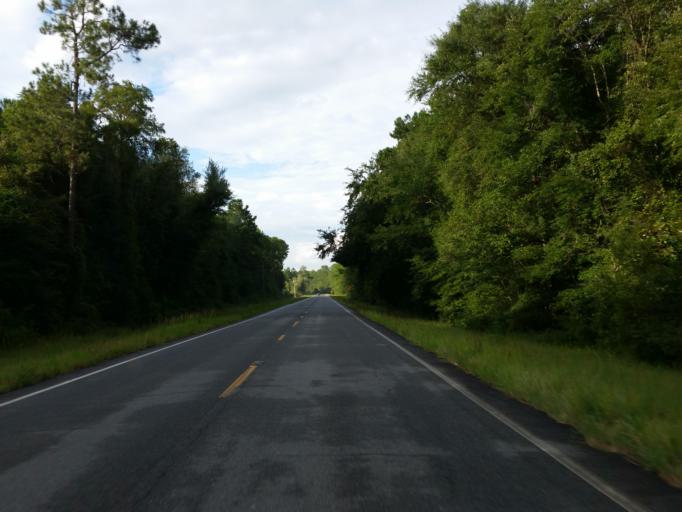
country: US
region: Georgia
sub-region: Clinch County
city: Homerville
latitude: 30.6663
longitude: -82.5567
